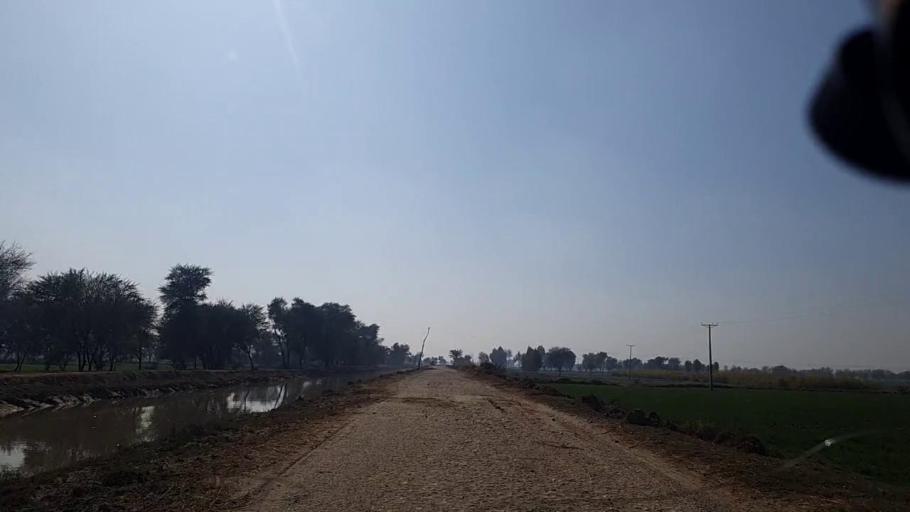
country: PK
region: Sindh
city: Khanpur
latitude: 27.8038
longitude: 69.4121
